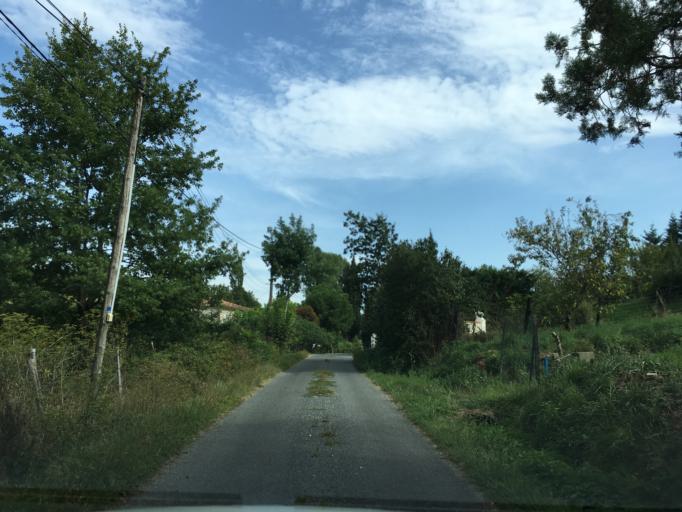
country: FR
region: Midi-Pyrenees
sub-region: Departement du Tarn
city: Lagarrigue
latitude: 43.6058
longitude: 2.2792
